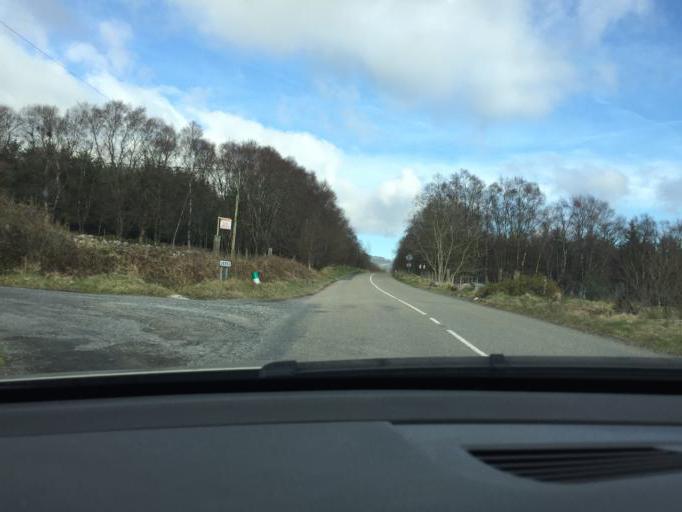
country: IE
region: Leinster
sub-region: Wicklow
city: Valleymount
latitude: 53.0601
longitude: -6.5030
